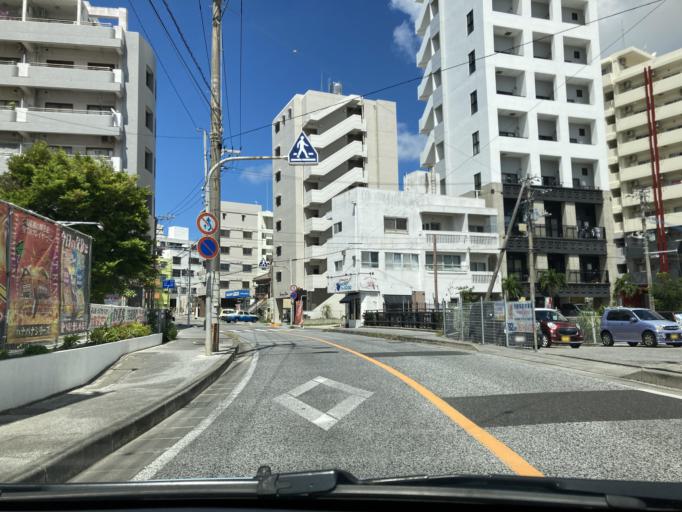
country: JP
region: Okinawa
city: Naha-shi
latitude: 26.2147
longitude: 127.6965
